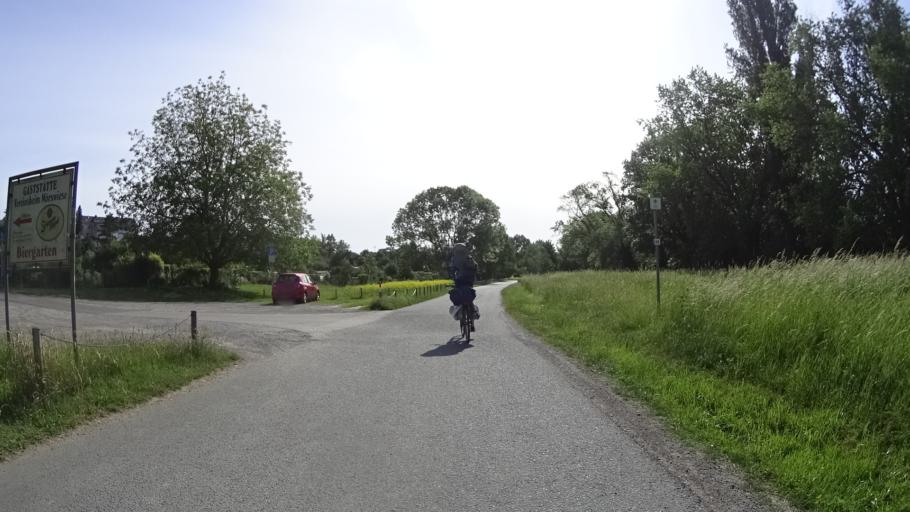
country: DE
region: Bavaria
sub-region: Regierungsbezirk Unterfranken
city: Aschaffenburg
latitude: 49.9787
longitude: 9.1225
